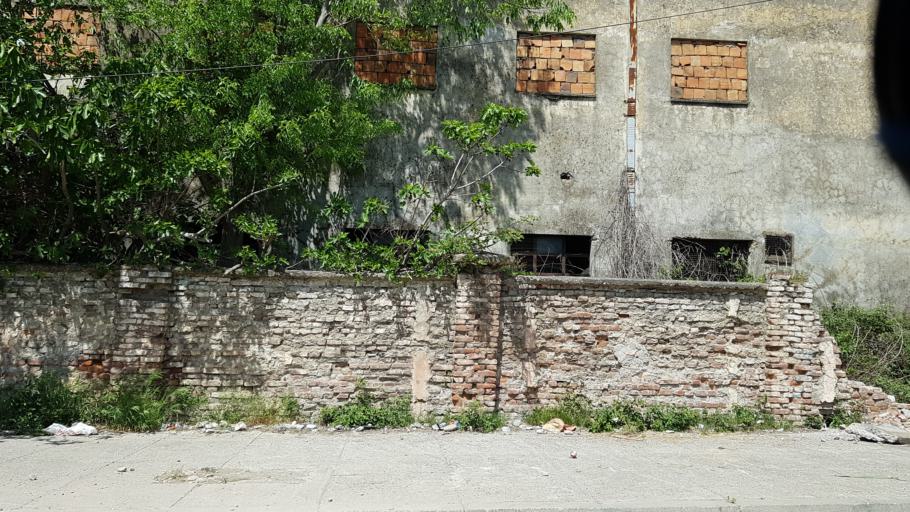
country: AL
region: Shkoder
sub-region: Rrethi i Shkodres
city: Shkoder
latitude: 42.0870
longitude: 19.5311
